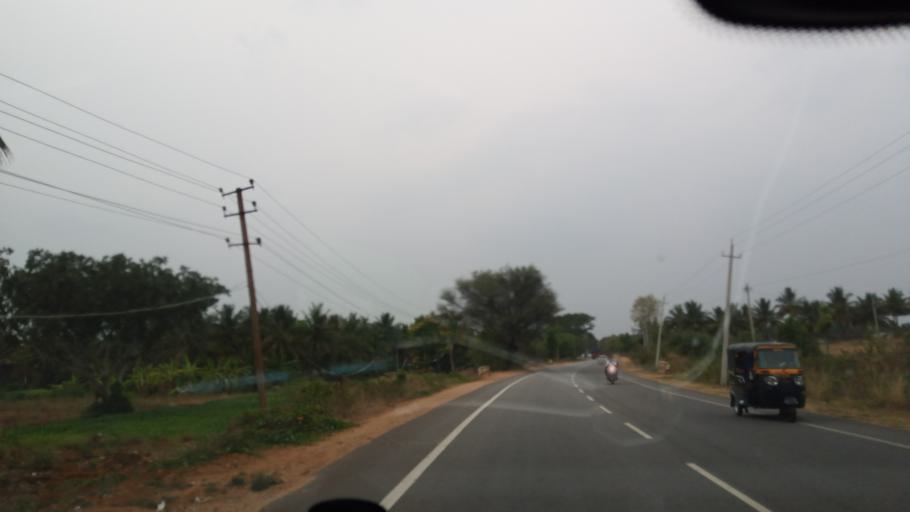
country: IN
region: Karnataka
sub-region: Mandya
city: Nagamangala
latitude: 12.8014
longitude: 76.7517
